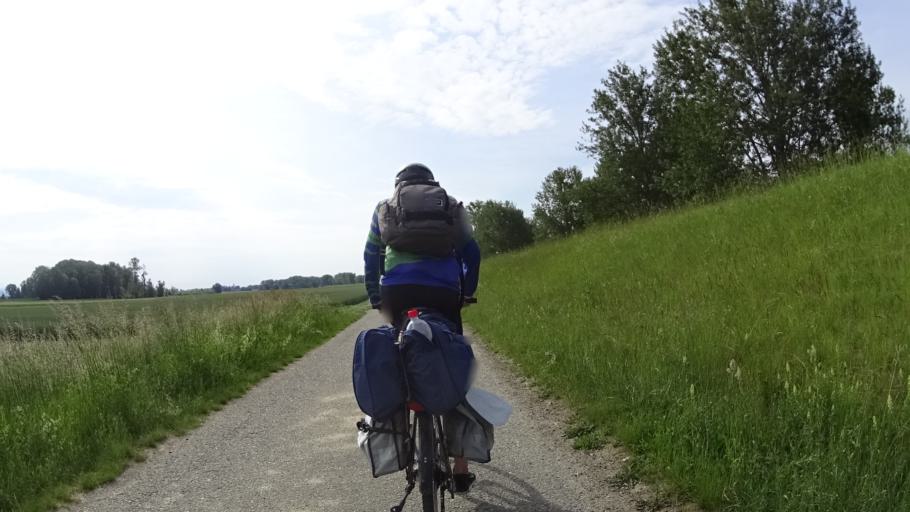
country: DE
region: Bavaria
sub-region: Lower Bavaria
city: Mariaposching
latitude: 48.8364
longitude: 12.7779
